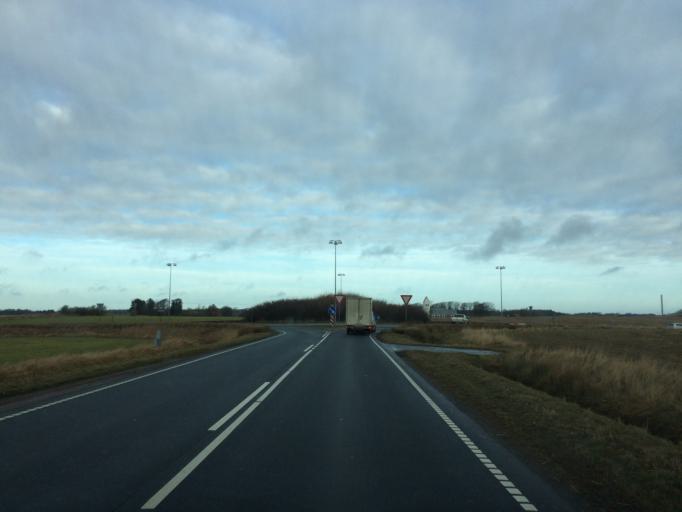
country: DK
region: Central Jutland
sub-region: Struer Kommune
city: Struer
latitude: 56.4666
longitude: 8.5468
